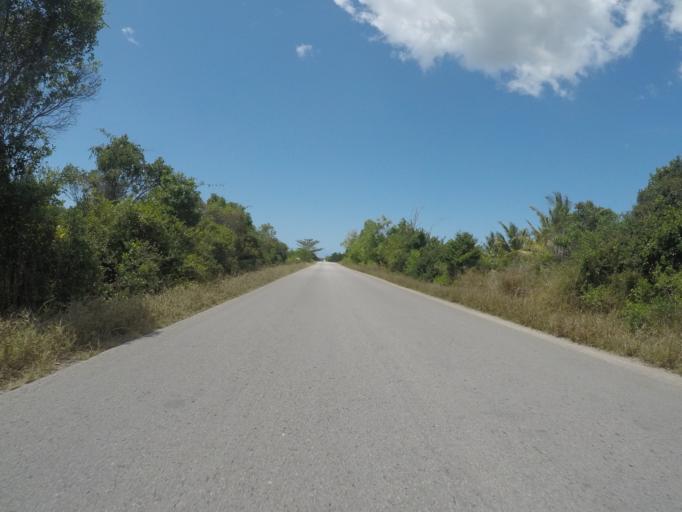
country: TZ
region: Zanzibar Central/South
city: Nganane
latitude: -6.2793
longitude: 39.4784
